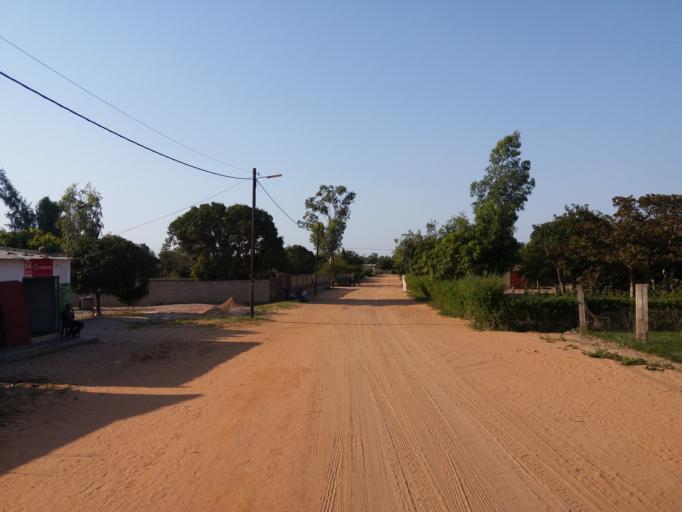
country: MZ
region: Maputo City
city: Maputo
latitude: -25.7634
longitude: 32.6087
